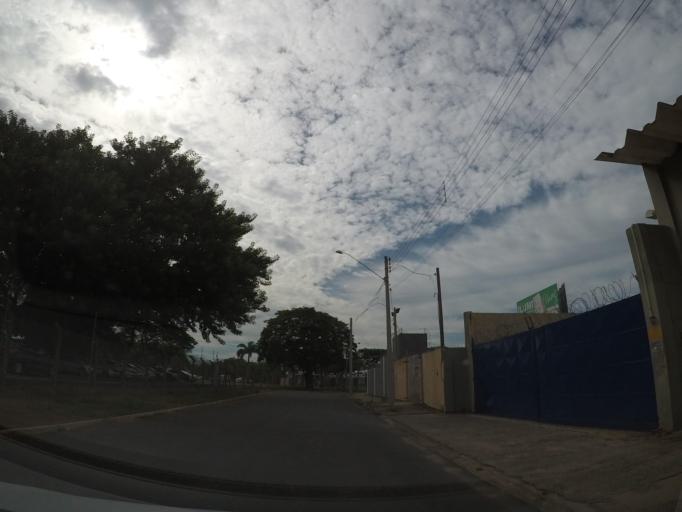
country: BR
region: Sao Paulo
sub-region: Hortolandia
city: Hortolandia
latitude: -22.8225
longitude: -47.1908
